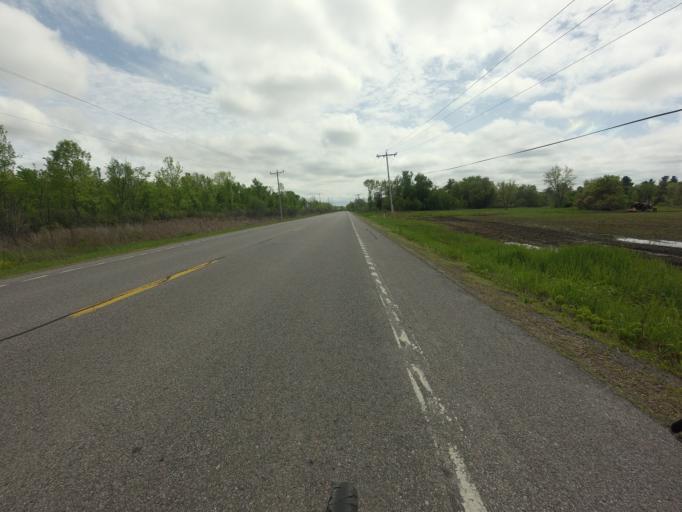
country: CA
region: Ontario
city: Cornwall
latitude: 44.9706
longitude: -74.6637
